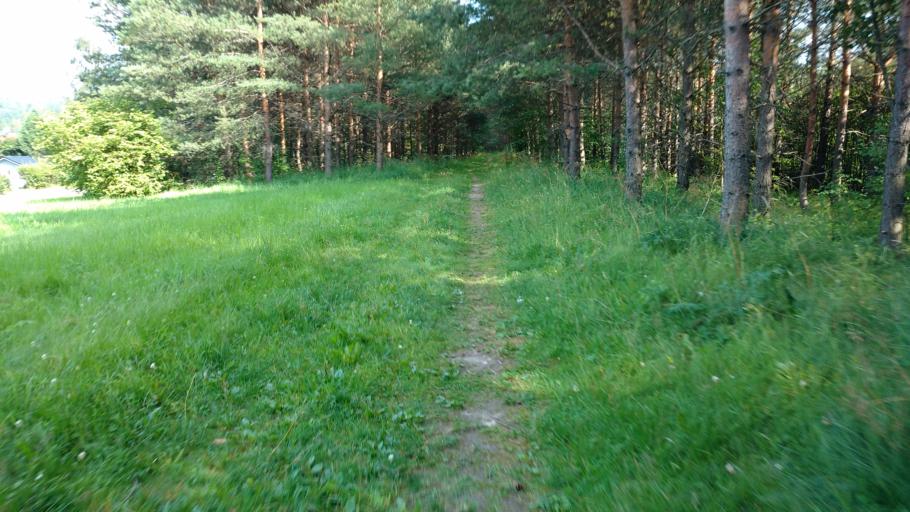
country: FI
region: Varsinais-Suomi
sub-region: Salo
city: Salo
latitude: 60.3895
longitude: 23.1578
